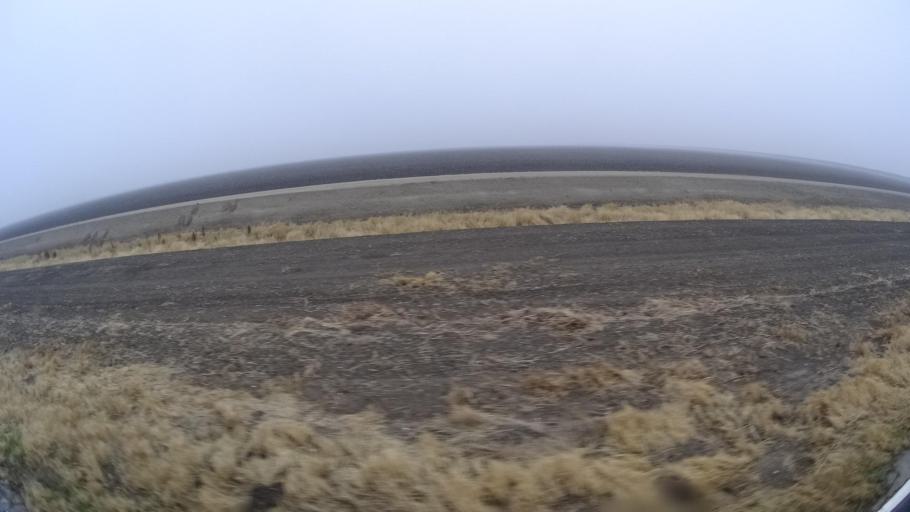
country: US
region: California
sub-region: Kern County
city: Lost Hills
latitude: 35.5527
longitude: -119.6180
